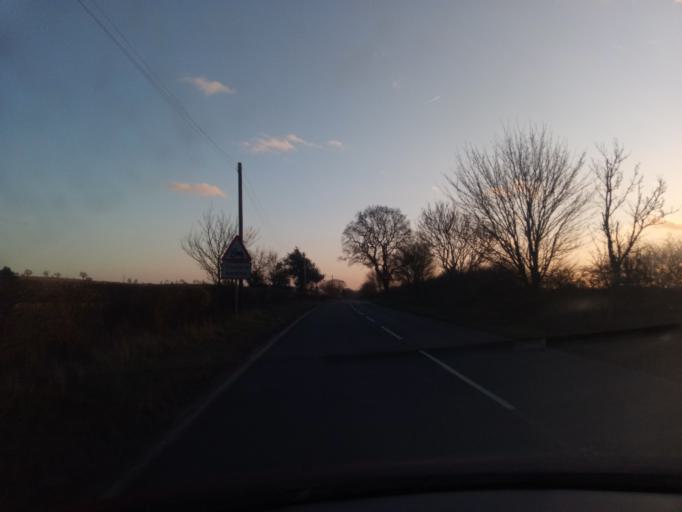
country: GB
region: England
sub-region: Nottinghamshire
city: Farnsfield
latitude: 53.0826
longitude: -1.0690
